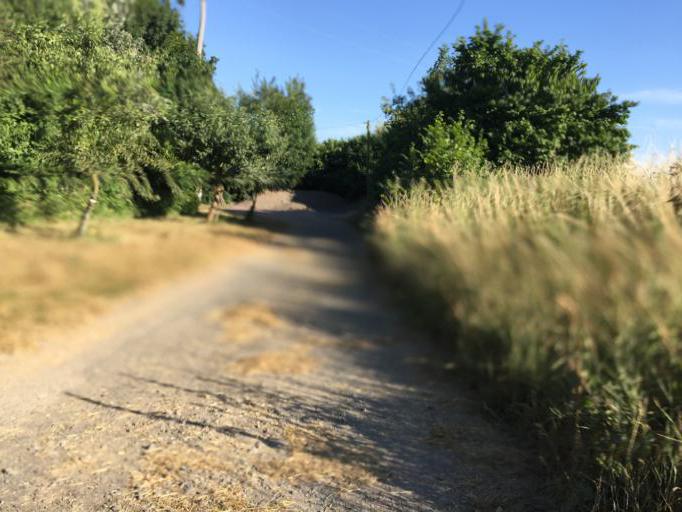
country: DE
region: Rheinland-Pfalz
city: Wallmerod
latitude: 50.4801
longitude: 7.9489
